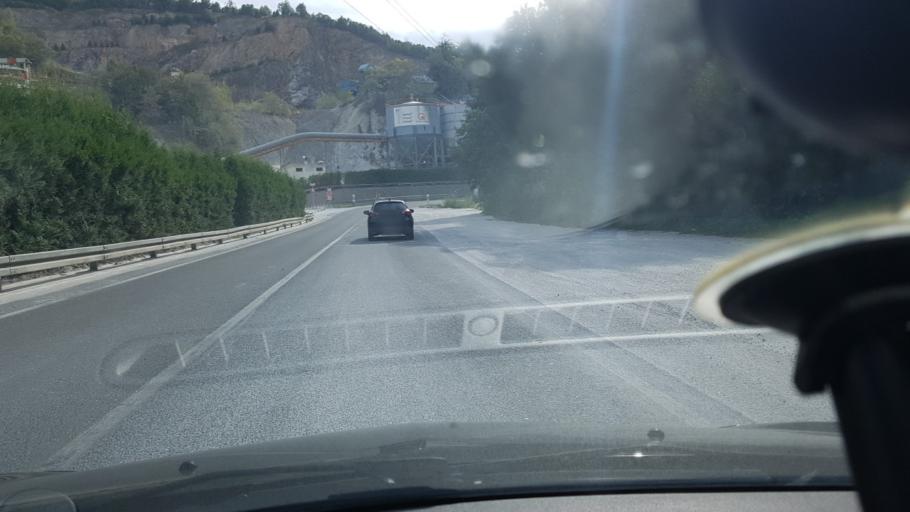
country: HR
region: Varazdinska
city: Lepoglava
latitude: 46.1946
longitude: 15.9935
